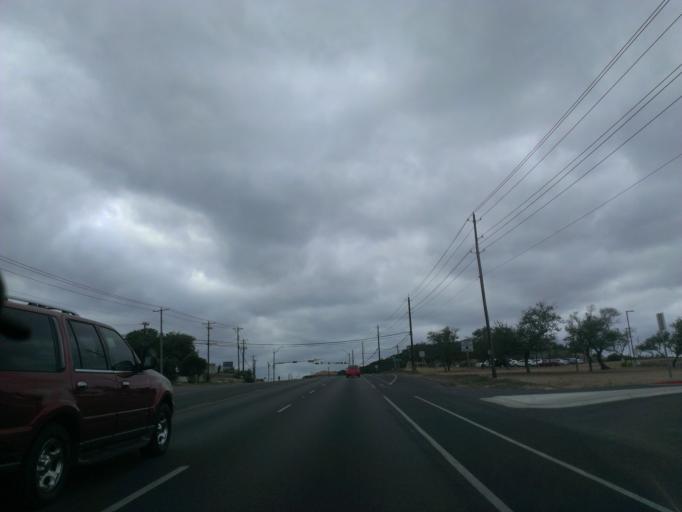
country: US
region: Texas
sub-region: Travis County
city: Lakeway
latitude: 30.3667
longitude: -97.9509
